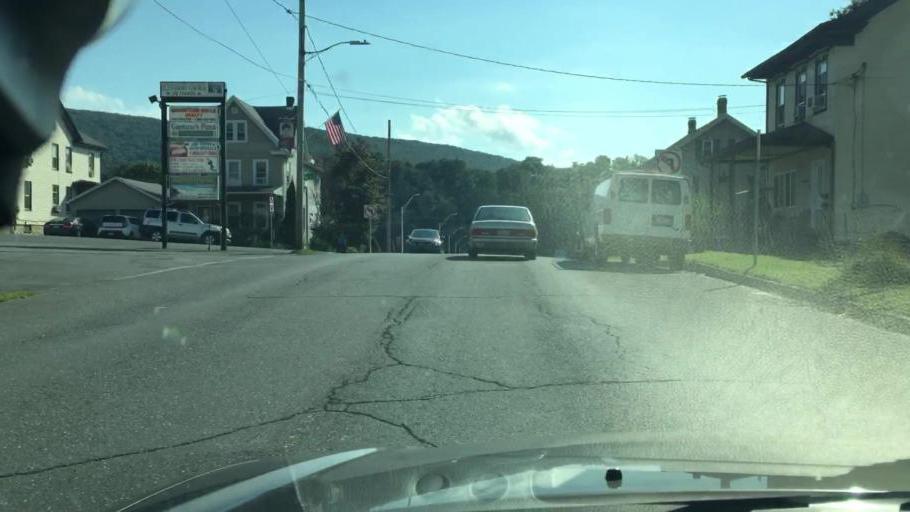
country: US
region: Pennsylvania
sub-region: Carbon County
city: Jim Thorpe
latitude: 40.8718
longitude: -75.7358
